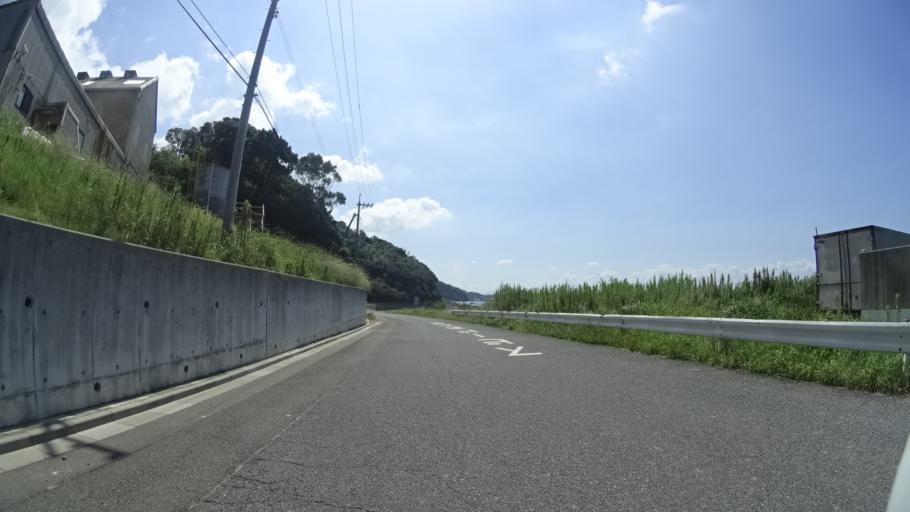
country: JP
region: Yamaguchi
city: Shimonoseki
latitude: 34.1025
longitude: 130.8691
